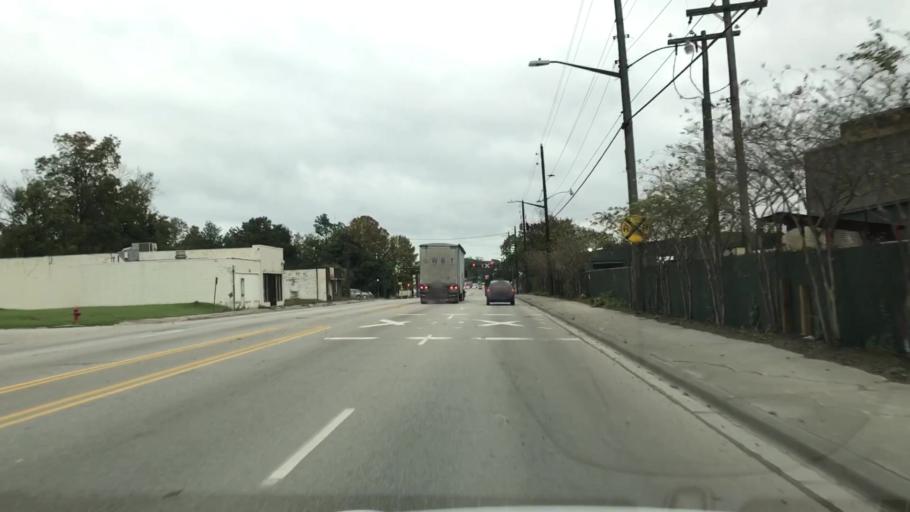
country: US
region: South Carolina
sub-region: Georgetown County
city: Georgetown
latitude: 33.3698
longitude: -79.2915
